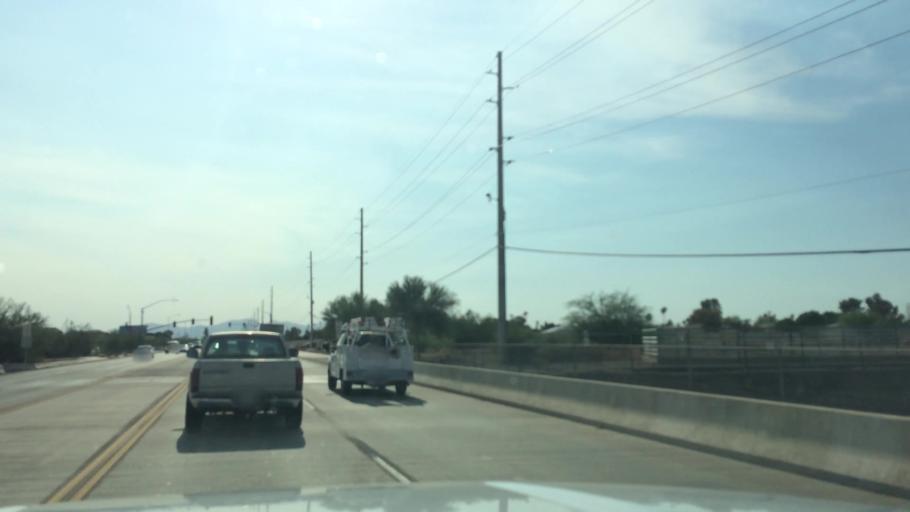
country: US
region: Arizona
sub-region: Maricopa County
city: Sun City
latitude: 33.5658
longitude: -112.2739
